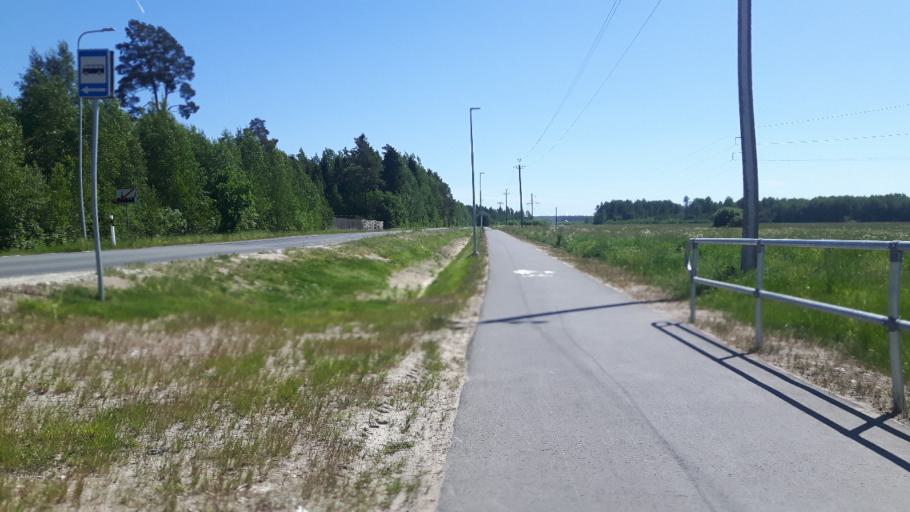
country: EE
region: Raplamaa
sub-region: Kohila vald
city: Kohila
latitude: 59.2127
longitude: 24.6807
